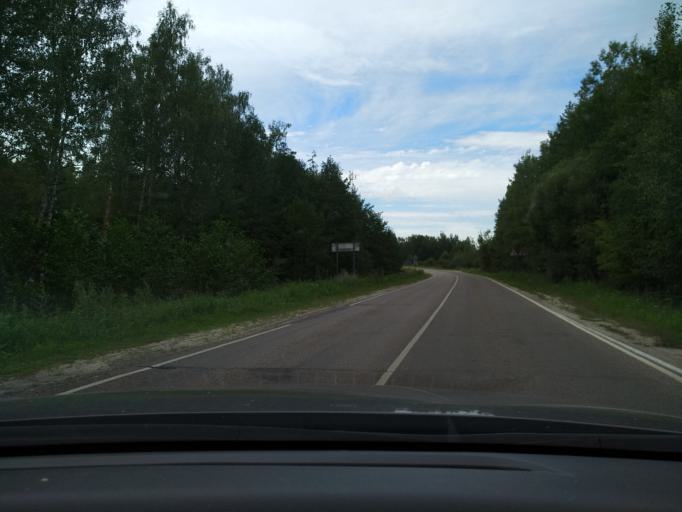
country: RU
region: Moskovskaya
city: Krasnyy Tkach
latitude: 55.3787
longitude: 39.2065
